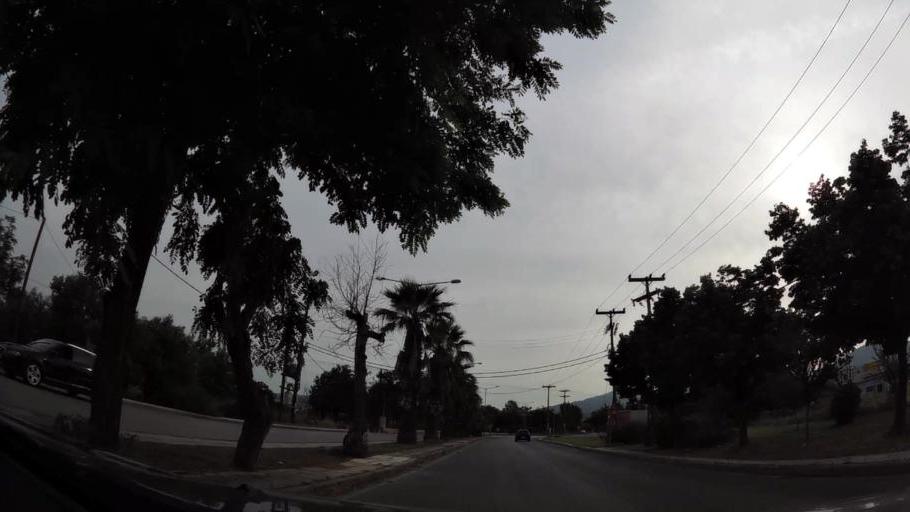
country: GR
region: Central Macedonia
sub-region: Nomos Thessalonikis
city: Thermi
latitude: 40.5405
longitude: 23.0148
